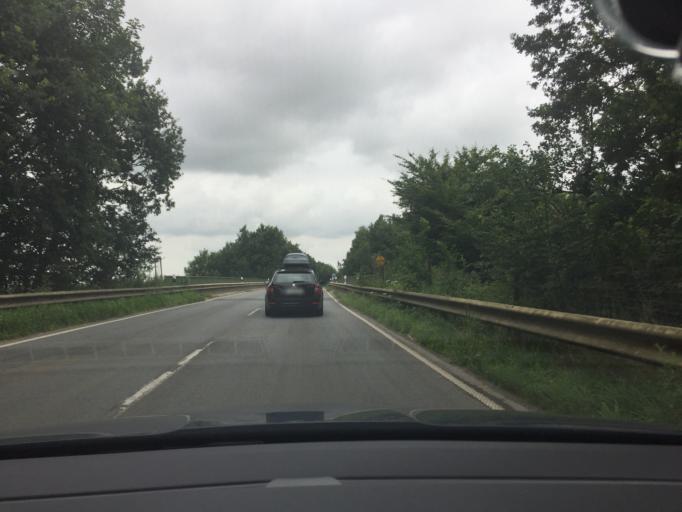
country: DE
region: Lower Saxony
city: Jemgum
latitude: 53.3668
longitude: 7.3477
